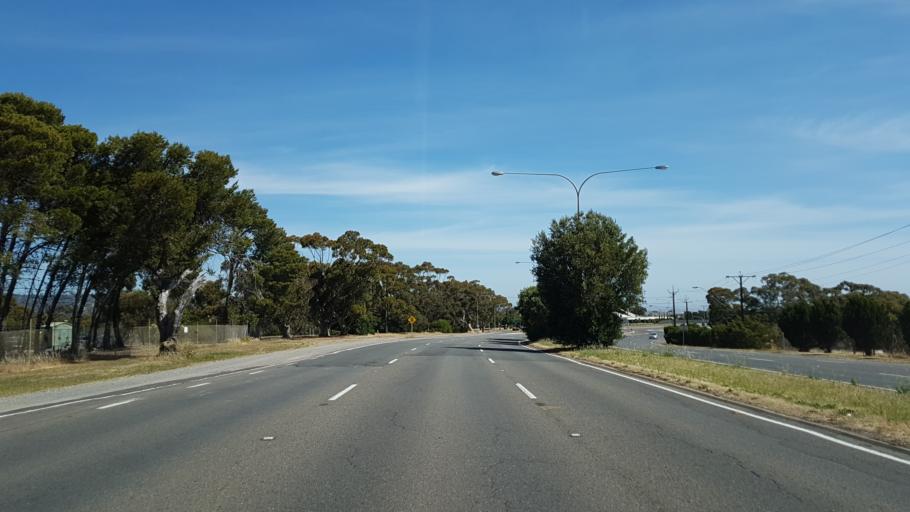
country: AU
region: South Australia
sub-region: Marion
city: Trott Park
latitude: -35.0581
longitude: 138.5600
